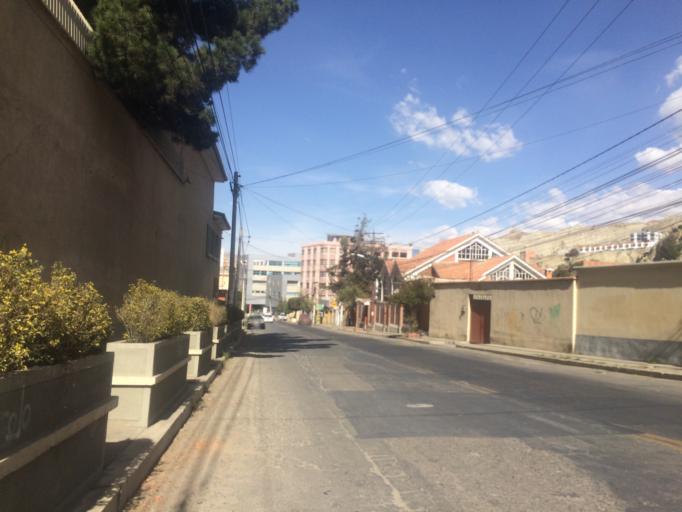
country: BO
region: La Paz
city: La Paz
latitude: -16.5234
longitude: -68.1141
